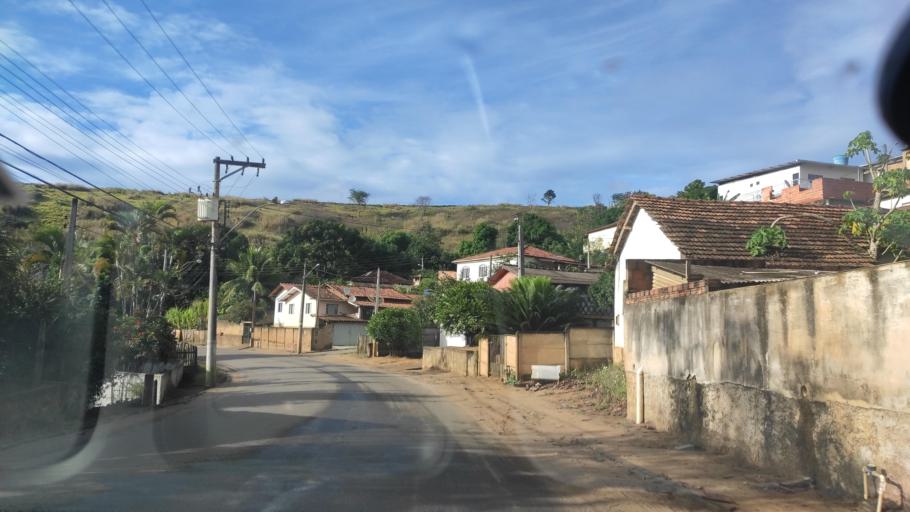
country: BR
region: Espirito Santo
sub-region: Nova Venecia
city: Nova Venecia
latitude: -18.7165
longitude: -40.3894
